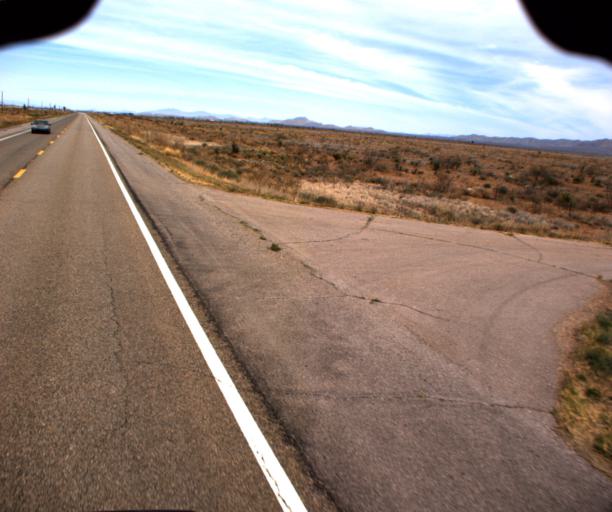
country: US
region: Arizona
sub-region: Cochise County
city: Pirtleville
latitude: 31.6191
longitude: -109.6711
